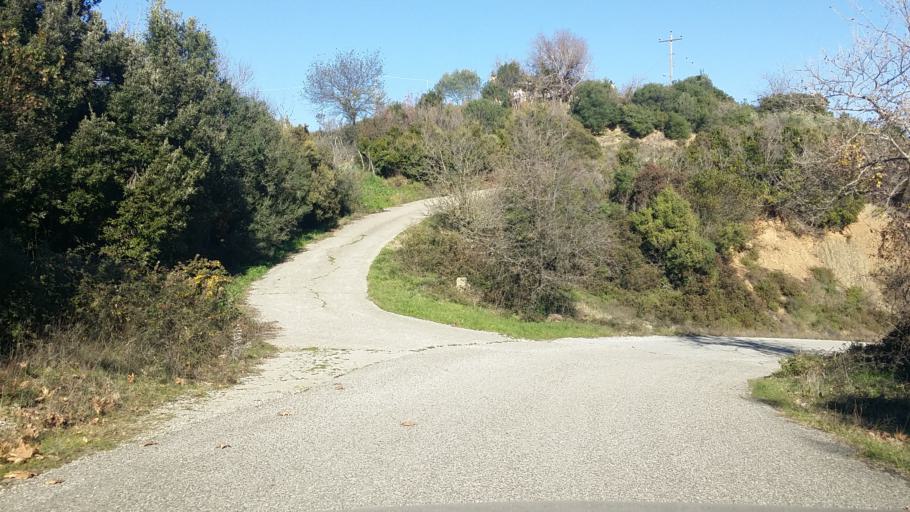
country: GR
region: West Greece
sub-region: Nomos Aitolias kai Akarnanias
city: Krikellos
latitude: 38.9995
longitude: 21.2387
